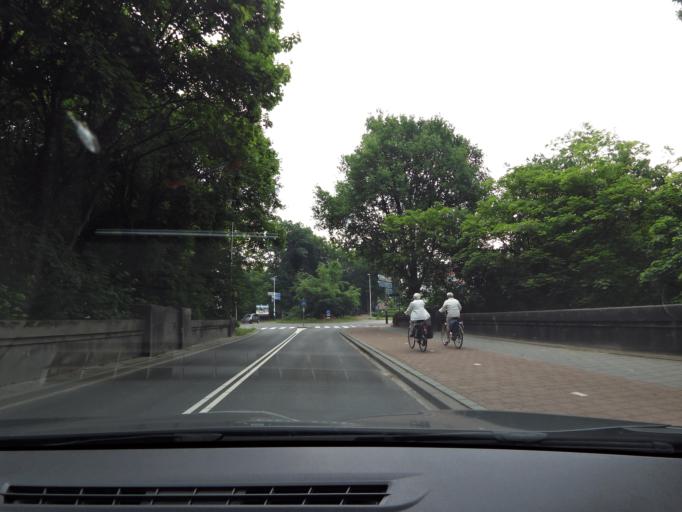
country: NL
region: Gelderland
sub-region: Gemeente Arnhem
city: Gulden Bodem
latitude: 52.0075
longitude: 5.9054
